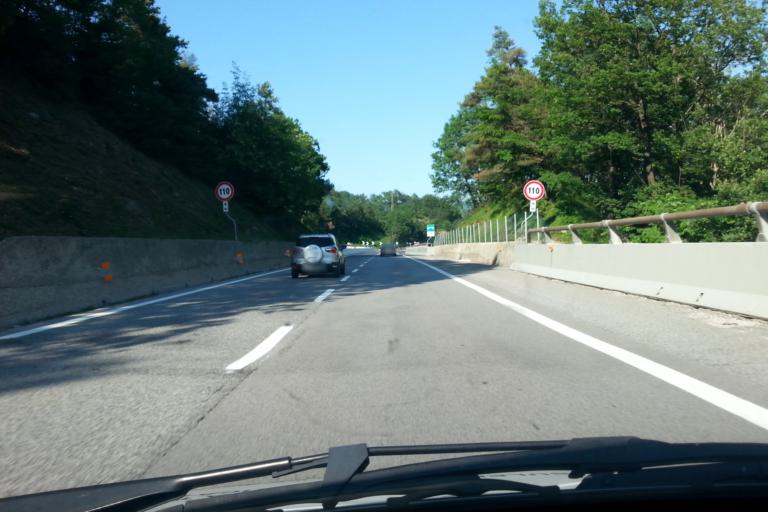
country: IT
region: Liguria
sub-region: Provincia di Savona
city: Plodio
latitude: 44.3667
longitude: 8.2560
